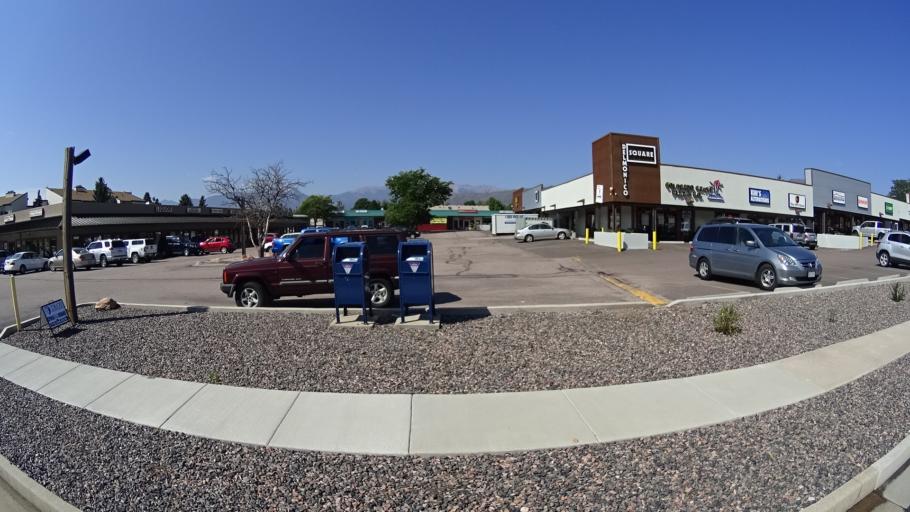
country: US
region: Colorado
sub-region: El Paso County
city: Air Force Academy
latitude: 38.9275
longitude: -104.8302
